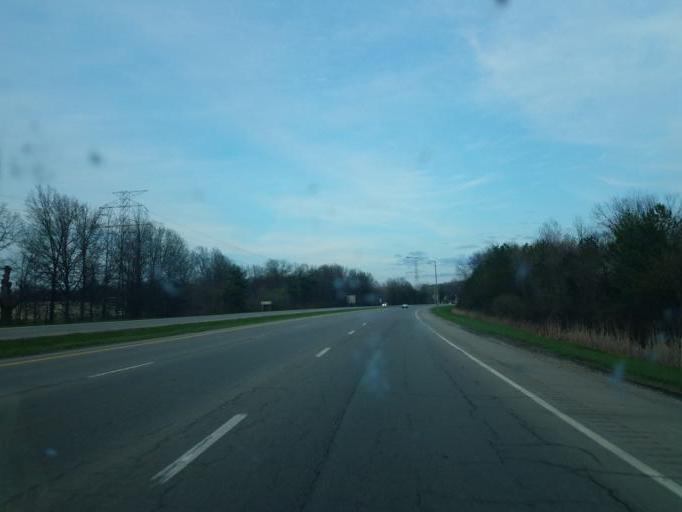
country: US
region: Ohio
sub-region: Lorain County
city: Amherst
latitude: 41.4142
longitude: -82.2025
